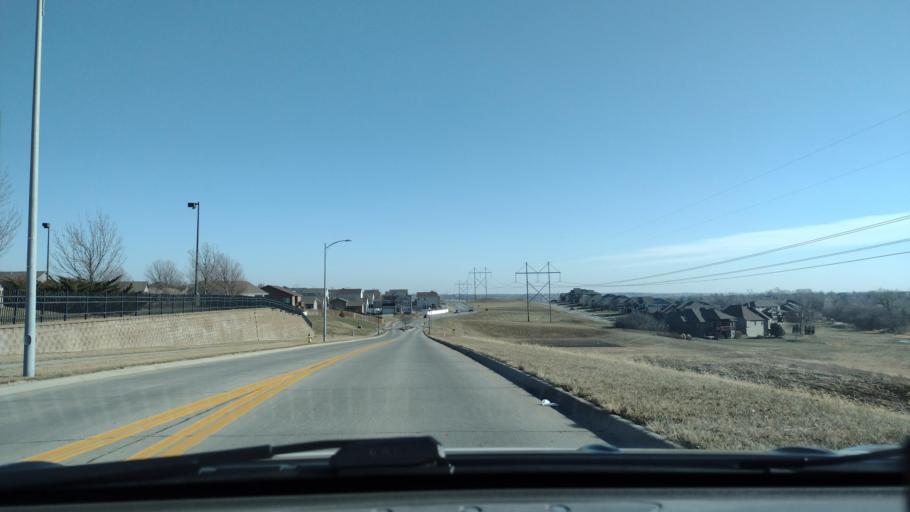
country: US
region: Nebraska
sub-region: Sarpy County
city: La Vista
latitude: 41.1696
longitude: -96.0205
